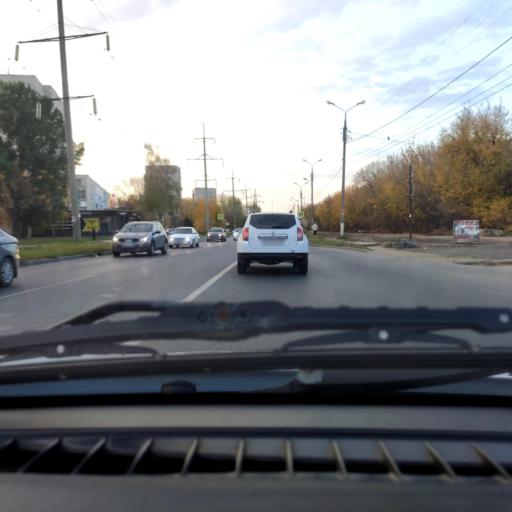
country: RU
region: Samara
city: Tol'yatti
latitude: 53.5282
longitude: 49.3964
